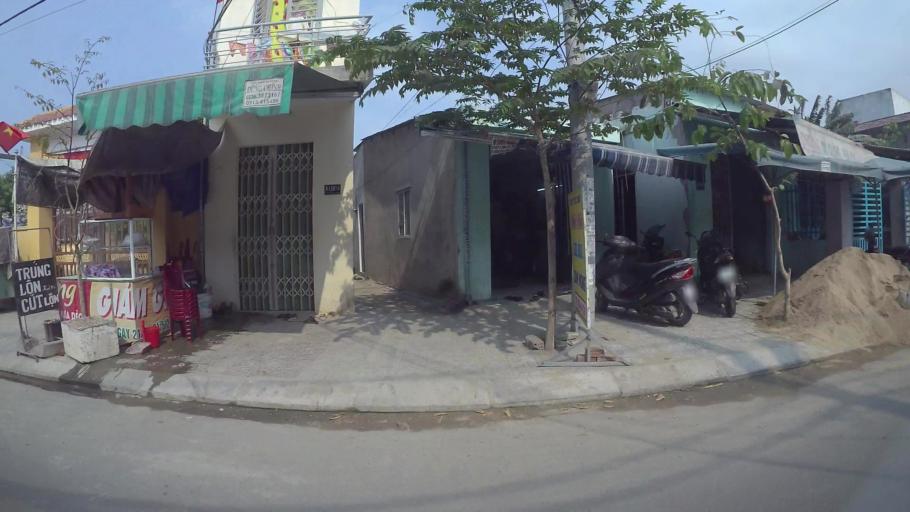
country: VN
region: Da Nang
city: Lien Chieu
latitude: 16.0539
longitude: 108.1564
